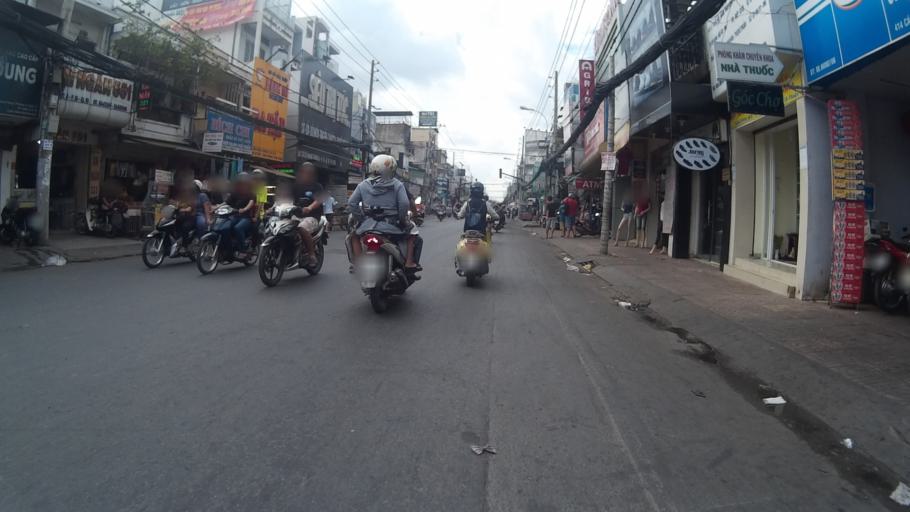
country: VN
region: Ho Chi Minh City
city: Quan Phu Nhuan
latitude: 10.7835
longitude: 106.6710
